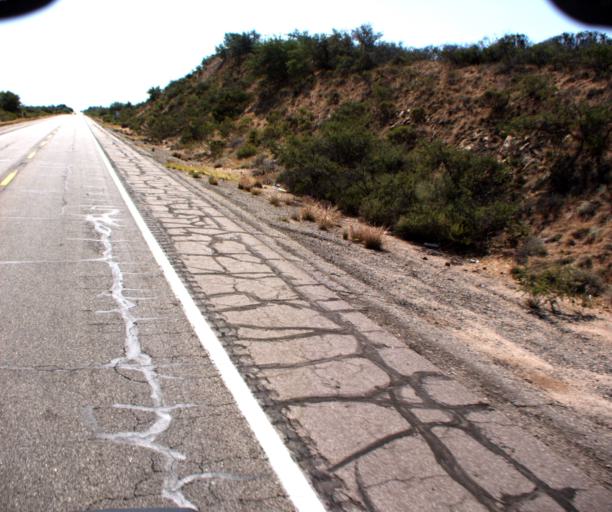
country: US
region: Arizona
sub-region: Pinal County
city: Oracle
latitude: 32.6232
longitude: -110.7740
